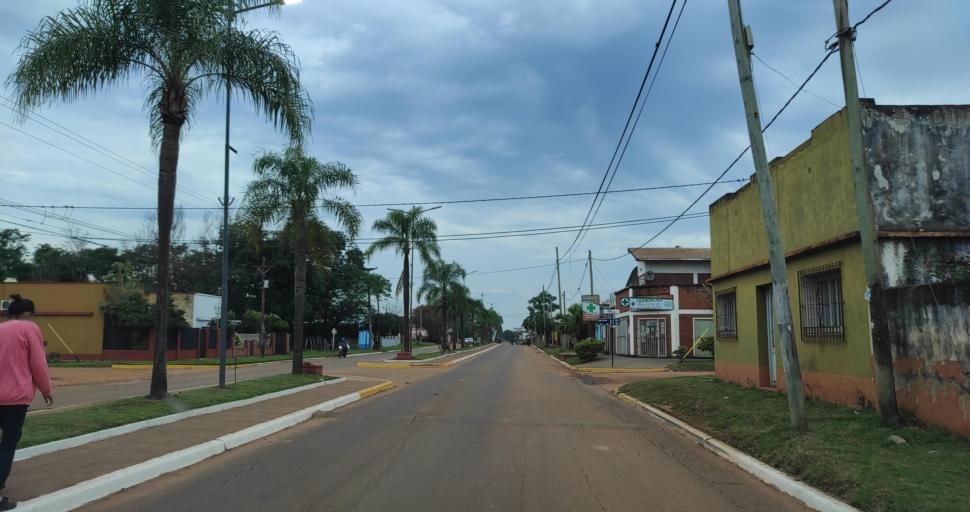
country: AR
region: Corrientes
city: Santo Tome
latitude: -28.5480
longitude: -56.0579
